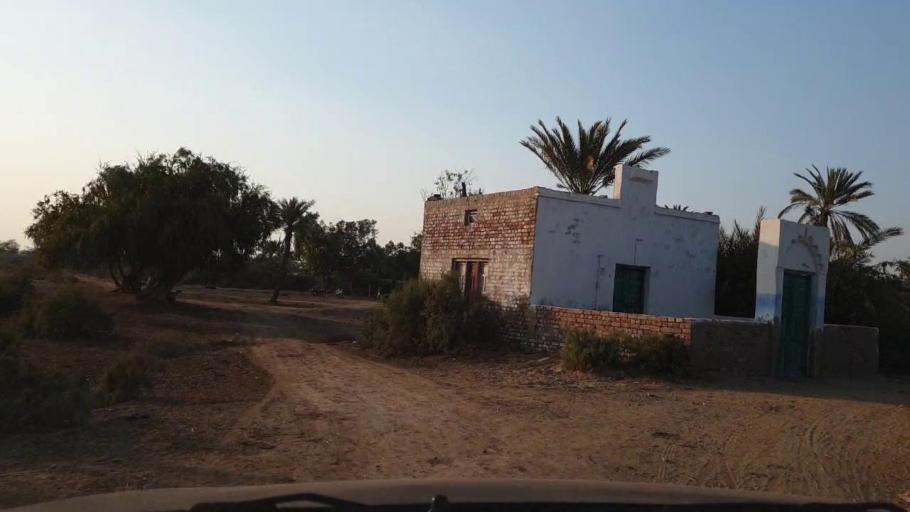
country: PK
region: Sindh
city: Jhol
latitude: 25.9310
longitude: 68.9250
